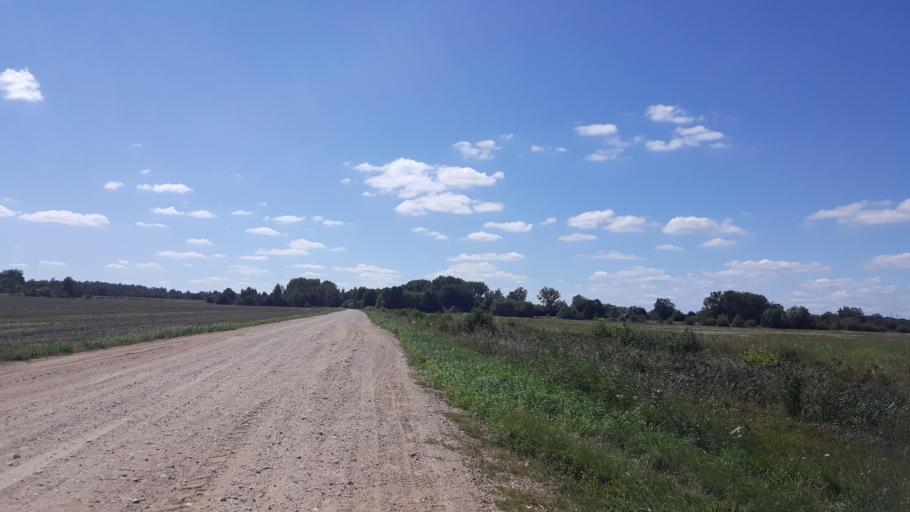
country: BY
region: Brest
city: Horad Kobryn
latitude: 52.3068
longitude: 24.3726
